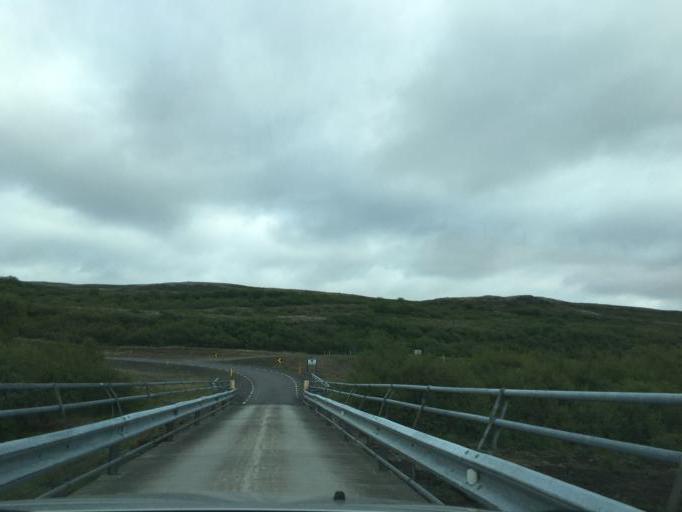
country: IS
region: South
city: Vestmannaeyjar
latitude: 64.2613
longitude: -20.2234
